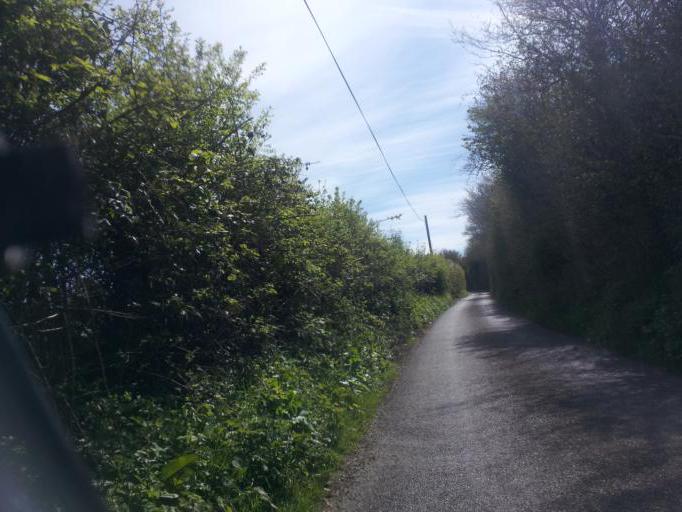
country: GB
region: England
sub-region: Kent
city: Rainham
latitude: 51.3160
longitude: 0.6134
